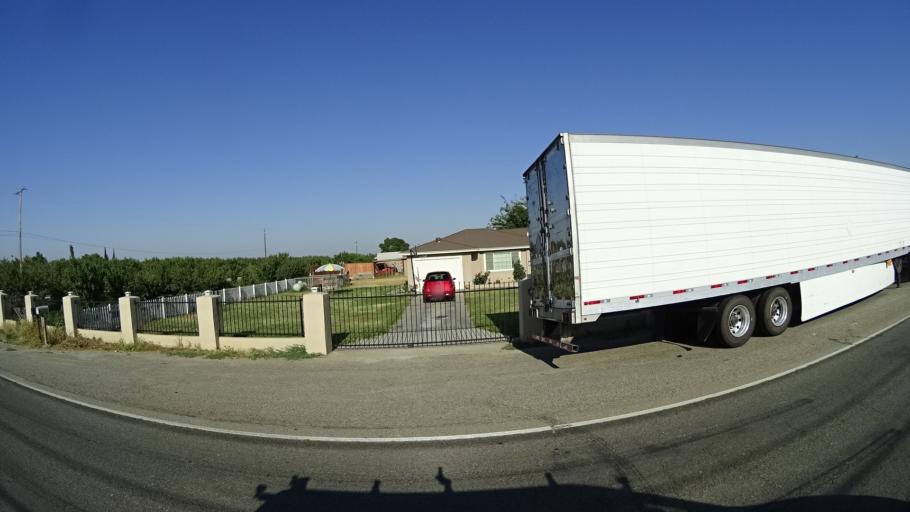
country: US
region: California
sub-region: Kings County
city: Lucerne
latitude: 36.3648
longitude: -119.7090
